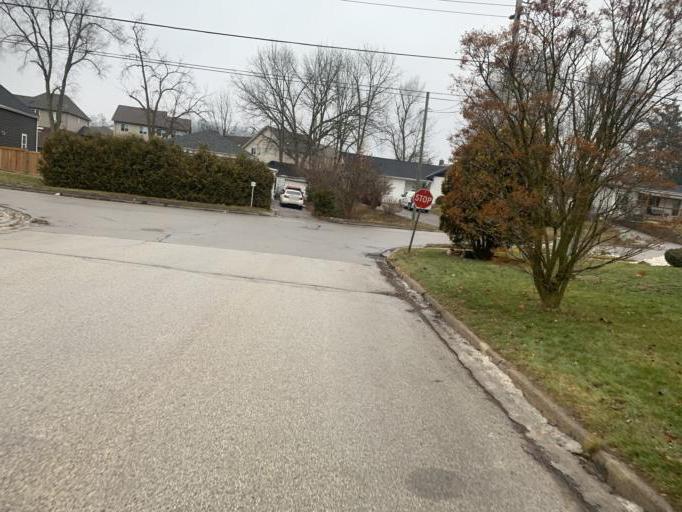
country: CA
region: Ontario
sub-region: Halton
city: Milton
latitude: 43.6596
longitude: -79.9174
